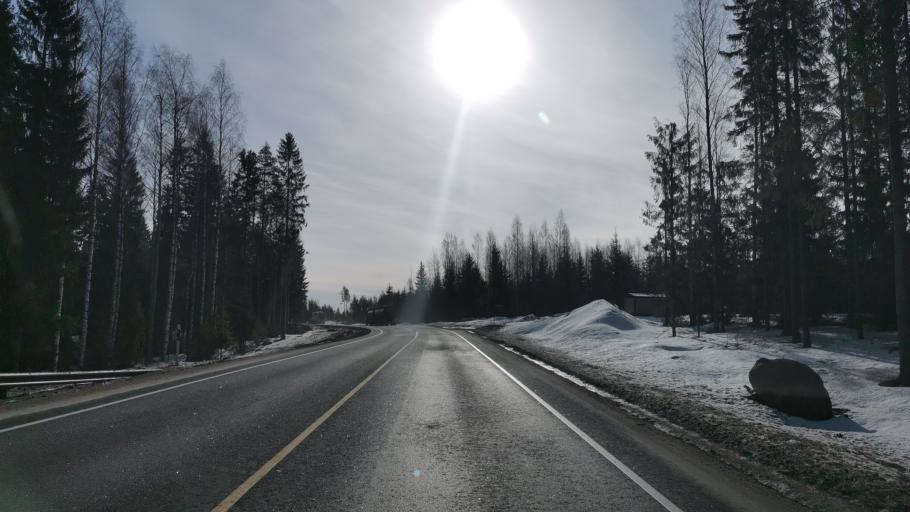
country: FI
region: Kymenlaakso
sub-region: Kouvola
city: Elimaeki
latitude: 60.8726
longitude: 26.5212
